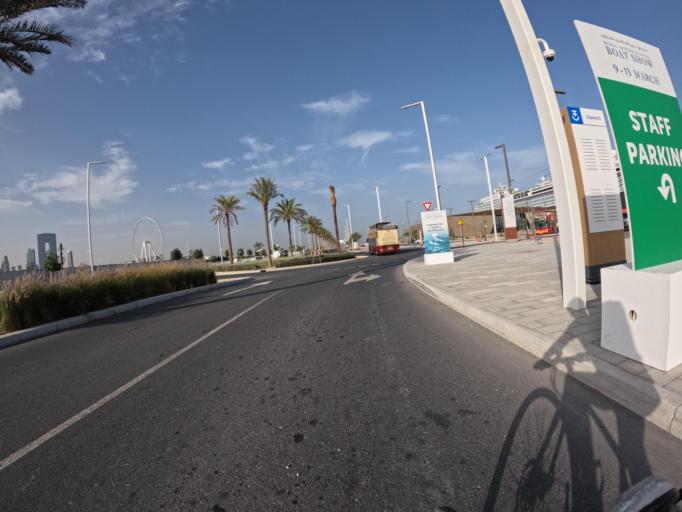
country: AE
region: Dubai
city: Dubai
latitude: 25.0928
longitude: 55.1314
